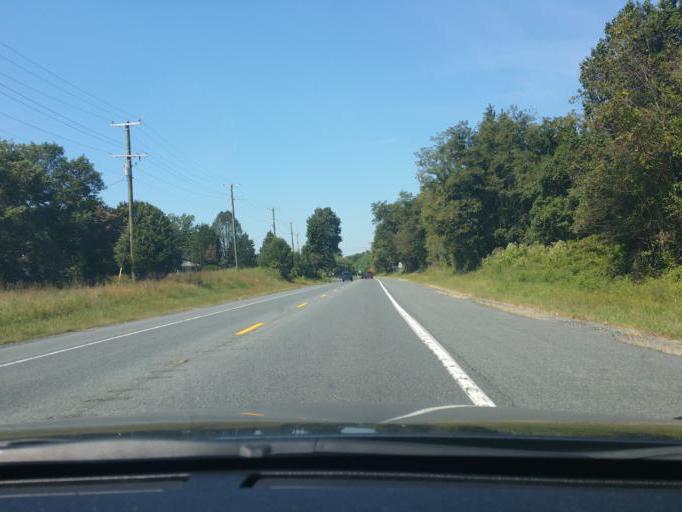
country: US
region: Maryland
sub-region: Harford County
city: Aberdeen
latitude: 39.5747
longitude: -76.1822
